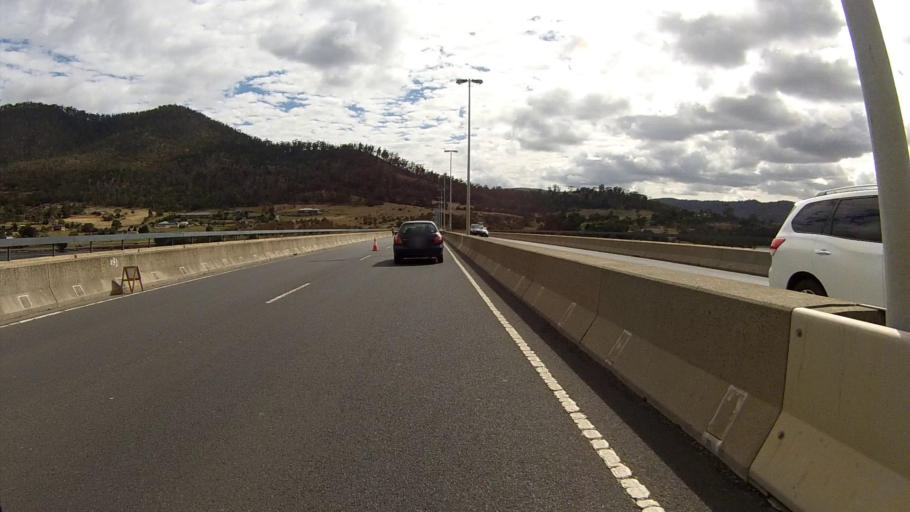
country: AU
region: Tasmania
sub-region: Glenorchy
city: Lutana
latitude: -42.8171
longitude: 147.3078
